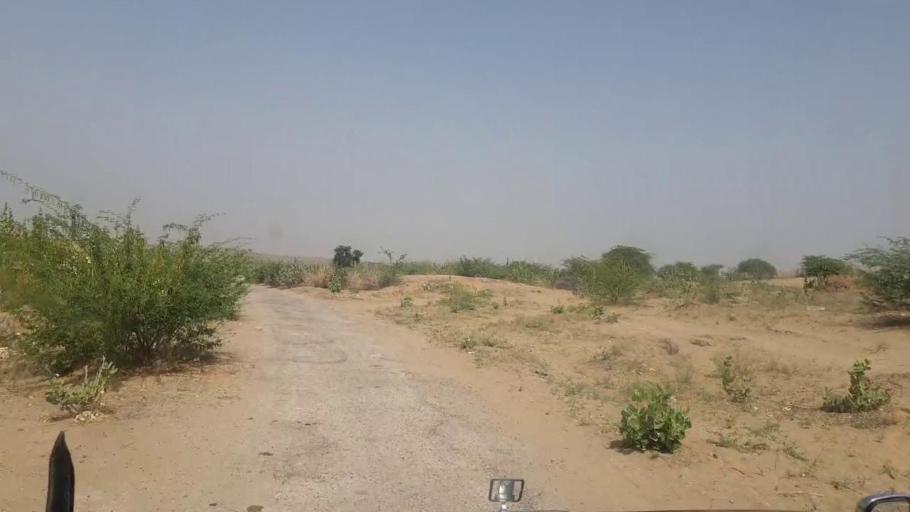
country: PK
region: Sindh
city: Islamkot
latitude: 25.1800
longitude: 70.1966
